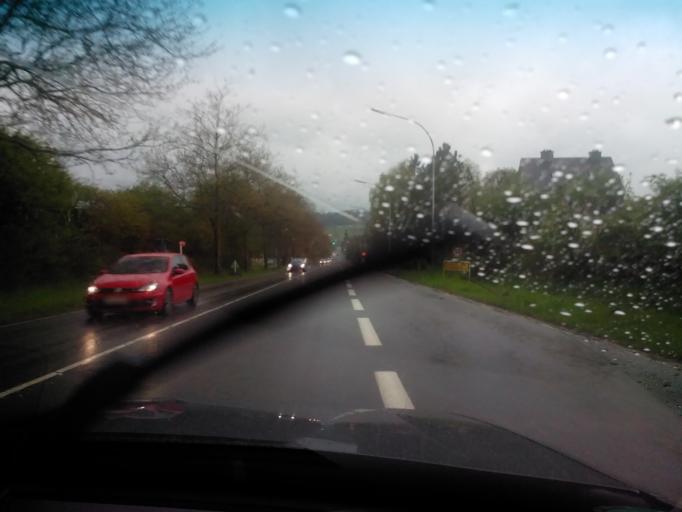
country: LU
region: Grevenmacher
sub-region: Canton de Grevenmacher
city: Junglinster
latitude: 49.7162
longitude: 6.2634
